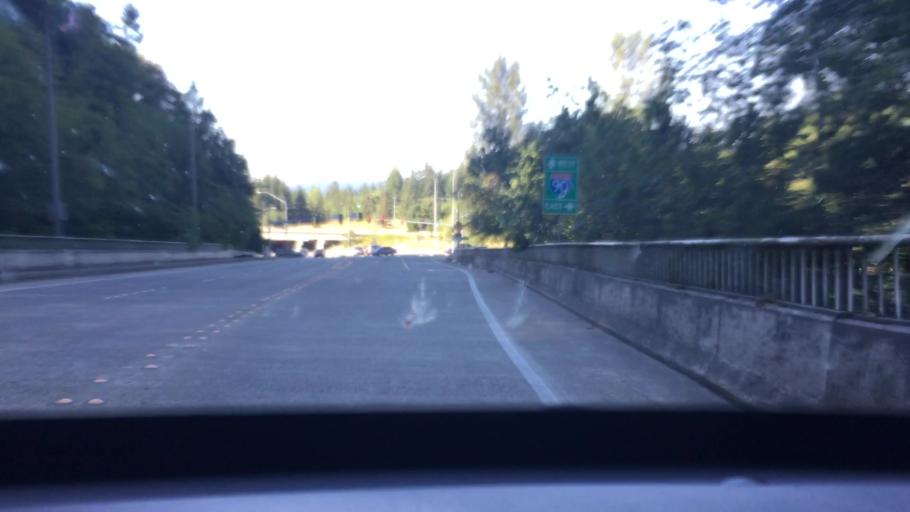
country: US
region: Washington
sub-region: King County
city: West Lake Sammamish
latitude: 47.5618
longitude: -122.0997
